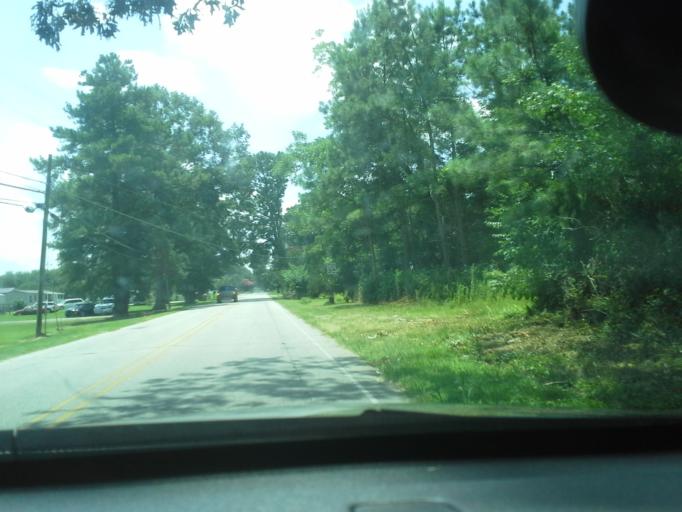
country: US
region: North Carolina
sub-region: Washington County
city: Plymouth
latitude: 35.8537
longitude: -76.7563
